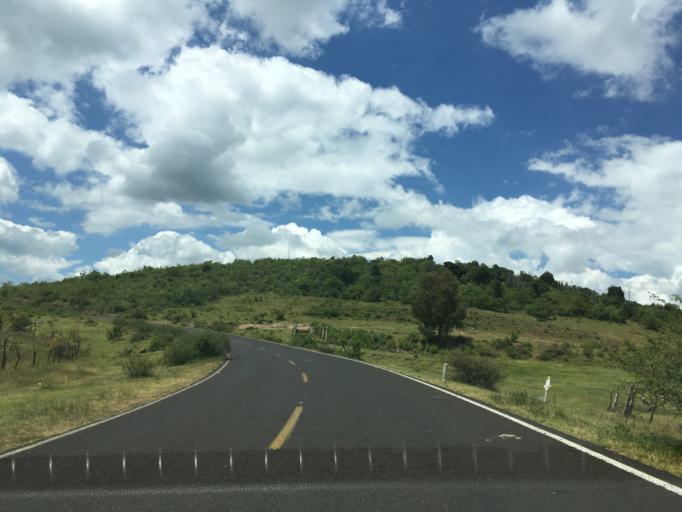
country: MX
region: Mexico
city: Huaniqueo de Morales
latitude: 19.8028
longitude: -101.4487
